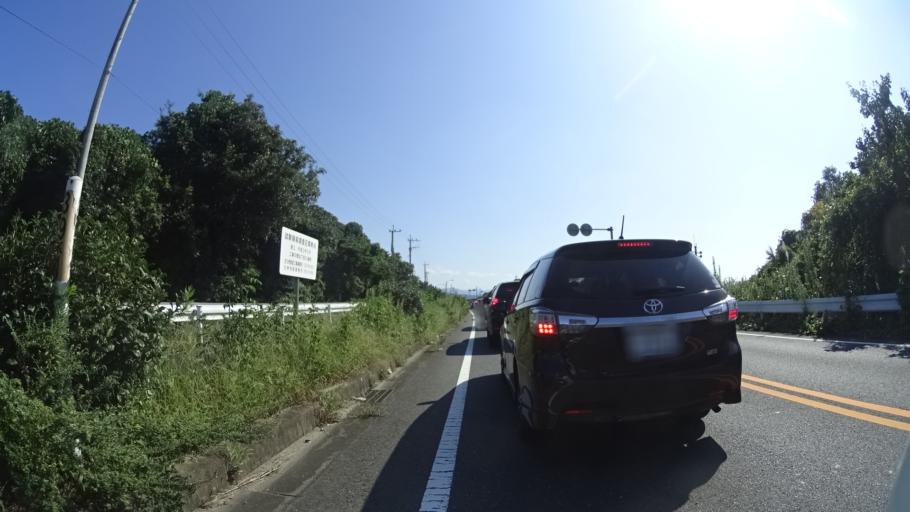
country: JP
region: Fukuoka
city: Yukuhashi
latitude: 33.6989
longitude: 130.9954
